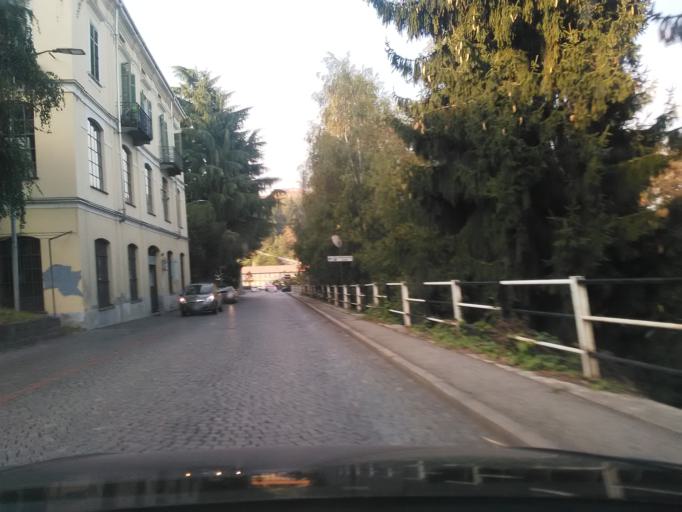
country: IT
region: Piedmont
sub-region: Provincia di Biella
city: Biella
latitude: 45.5688
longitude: 8.0604
